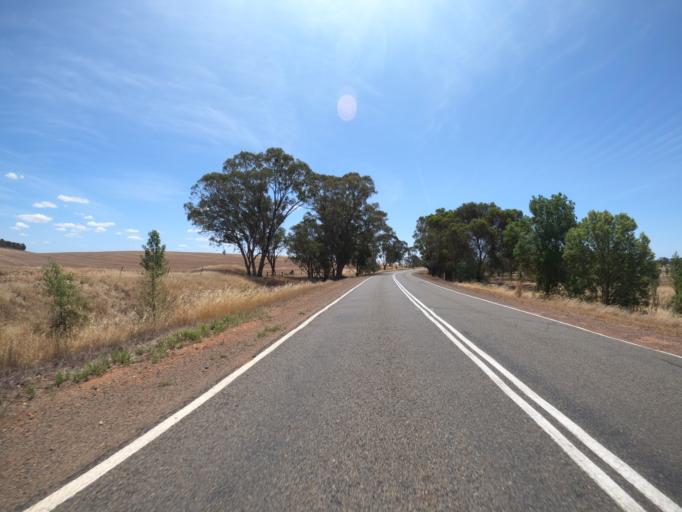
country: AU
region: Victoria
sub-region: Benalla
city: Benalla
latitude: -36.3239
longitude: 145.9590
